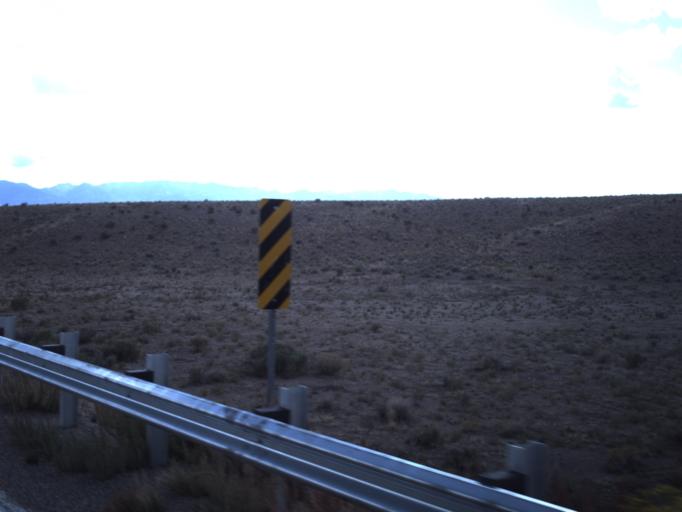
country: US
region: Utah
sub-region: Beaver County
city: Milford
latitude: 38.5678
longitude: -113.7780
